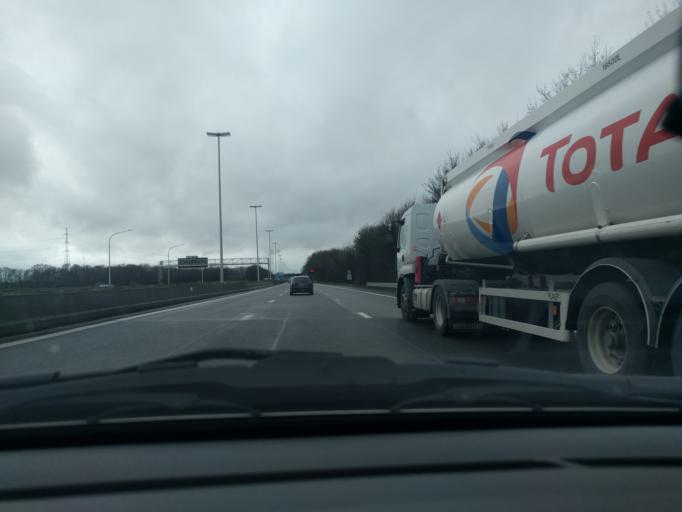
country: BE
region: Wallonia
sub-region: Province de Namur
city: Namur
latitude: 50.5169
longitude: 4.8675
